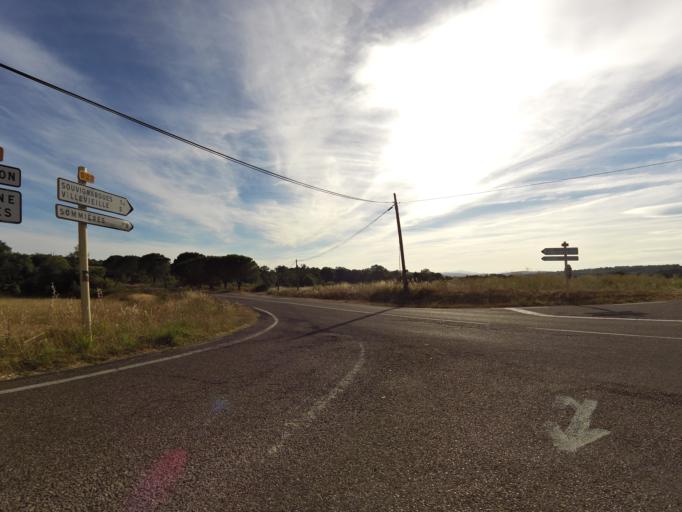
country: FR
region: Languedoc-Roussillon
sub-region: Departement du Gard
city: Villevieille
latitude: 43.8246
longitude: 4.1294
